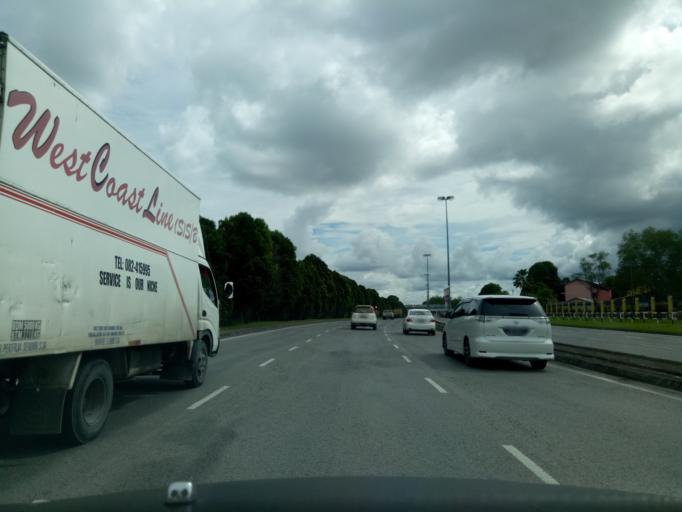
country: MY
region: Sarawak
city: Kuching
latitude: 1.5479
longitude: 110.3856
